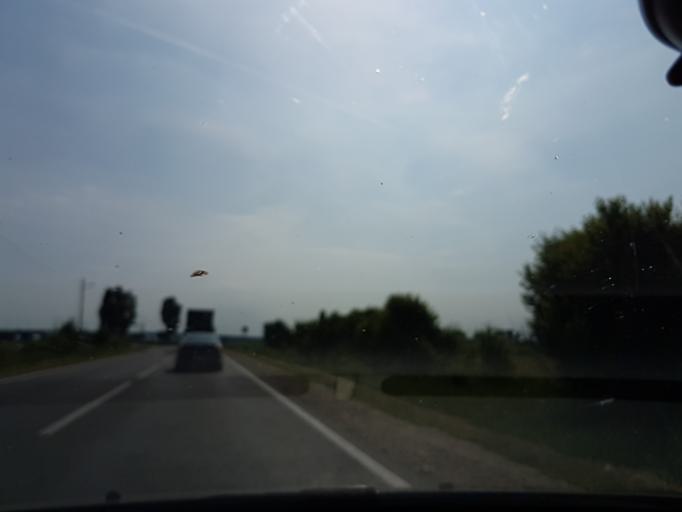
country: RO
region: Prahova
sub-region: Comuna Blejoiu
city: Ploiestiori
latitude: 44.9803
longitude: 25.9967
